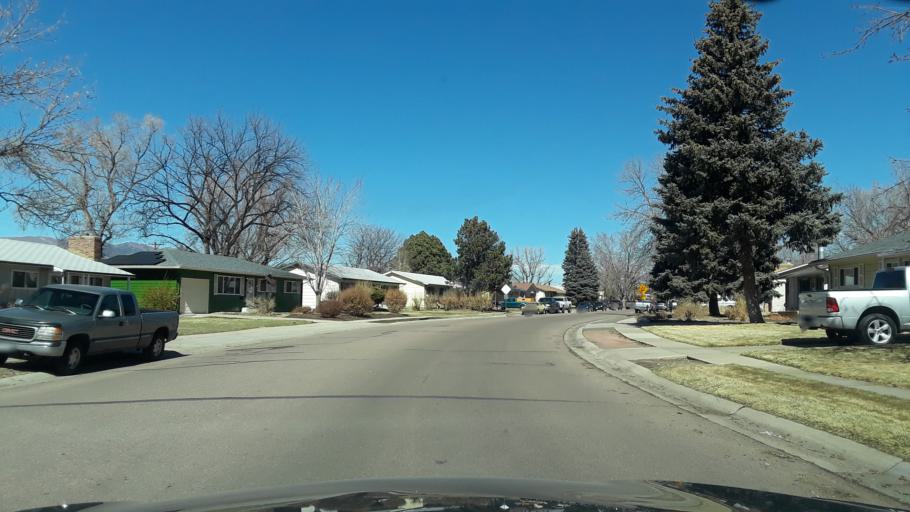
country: US
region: Colorado
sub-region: El Paso County
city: Colorado Springs
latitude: 38.8703
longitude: -104.8098
